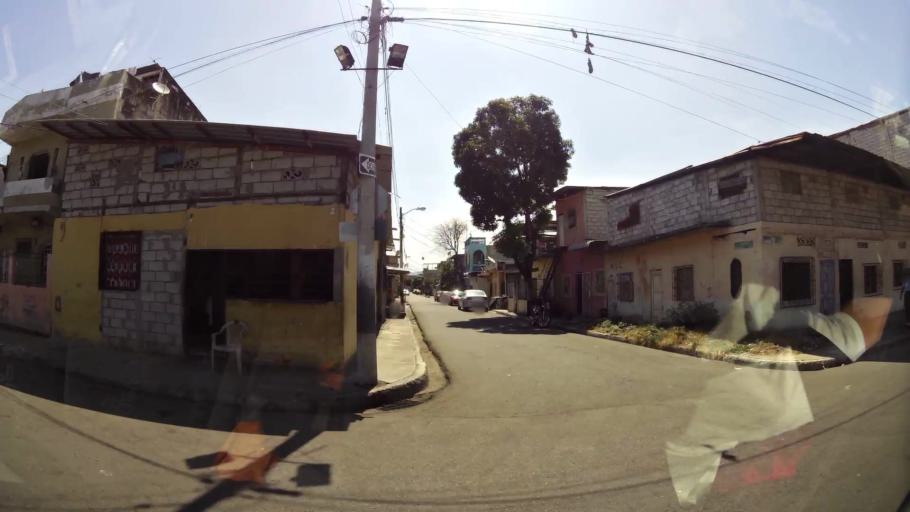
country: EC
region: Guayas
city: Guayaquil
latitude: -2.2247
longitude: -79.9365
